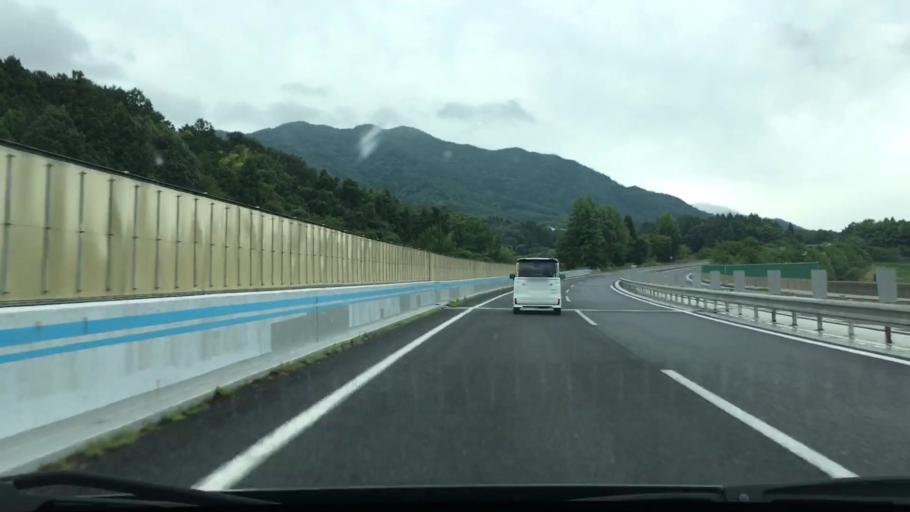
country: JP
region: Hiroshima
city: Hiroshima-shi
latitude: 34.6441
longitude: 132.5173
